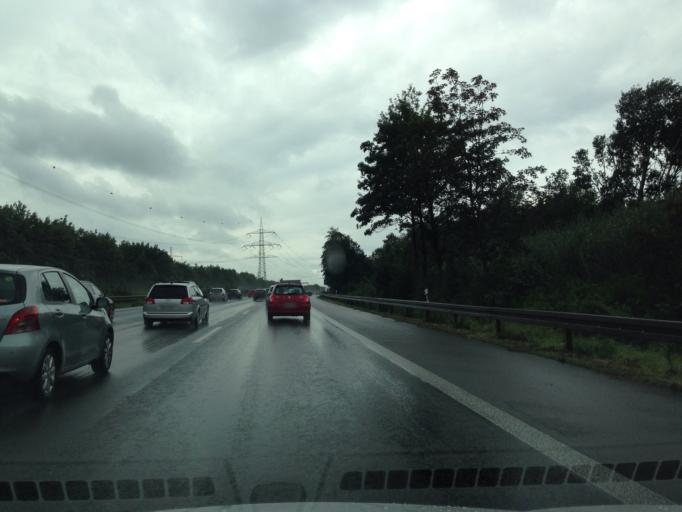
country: DE
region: North Rhine-Westphalia
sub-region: Regierungsbezirk Munster
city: Gladbeck
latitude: 51.5532
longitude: 6.9612
